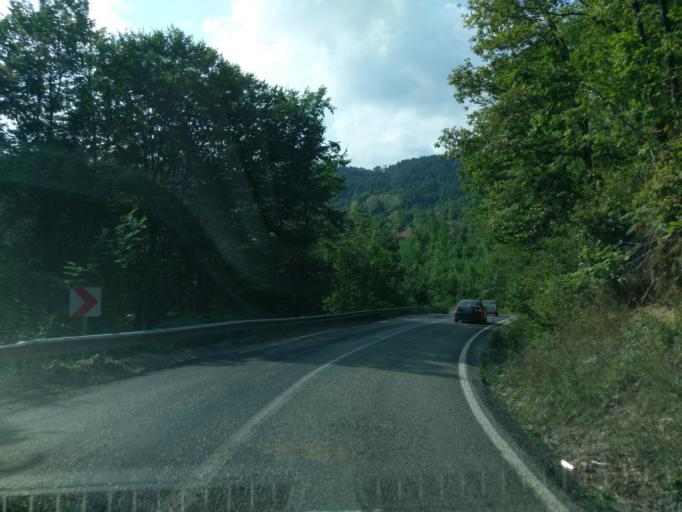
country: TR
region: Sinop
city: Ayancik
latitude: 41.8799
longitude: 34.5192
